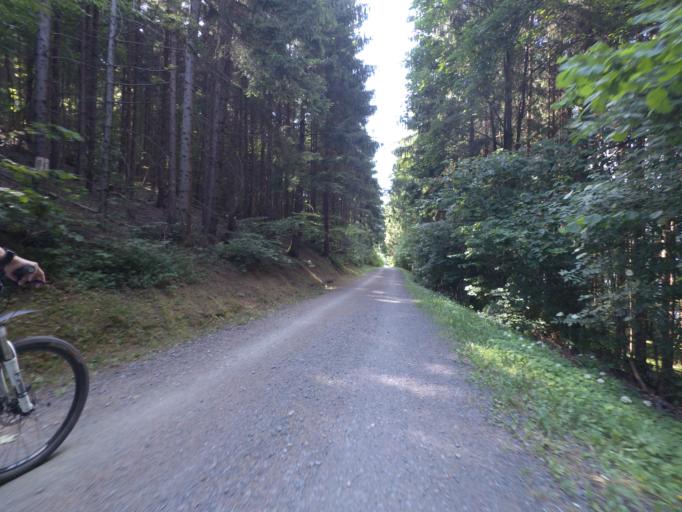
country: AT
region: Carinthia
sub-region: Politischer Bezirk Spittal an der Drau
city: Millstatt
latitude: 46.7745
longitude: 13.6003
